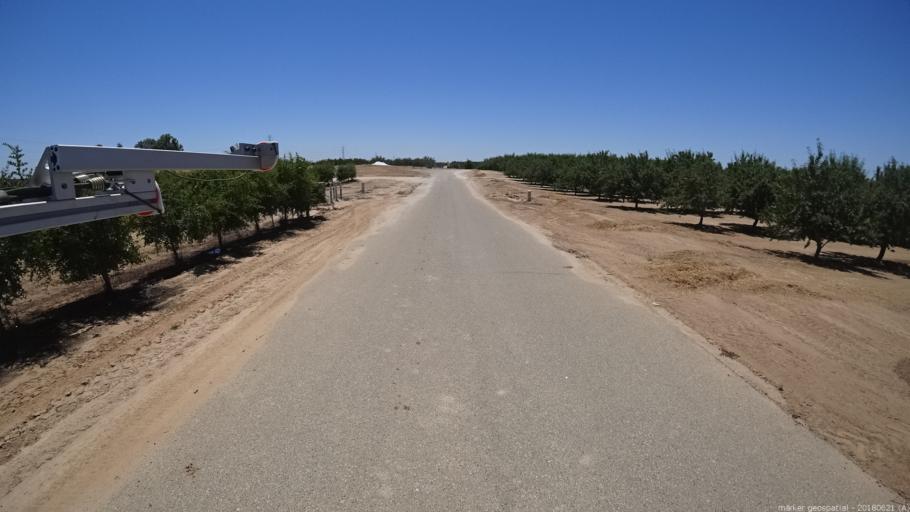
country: US
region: California
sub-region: Madera County
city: Bonadelle Ranchos-Madera Ranchos
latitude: 36.9020
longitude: -119.9166
